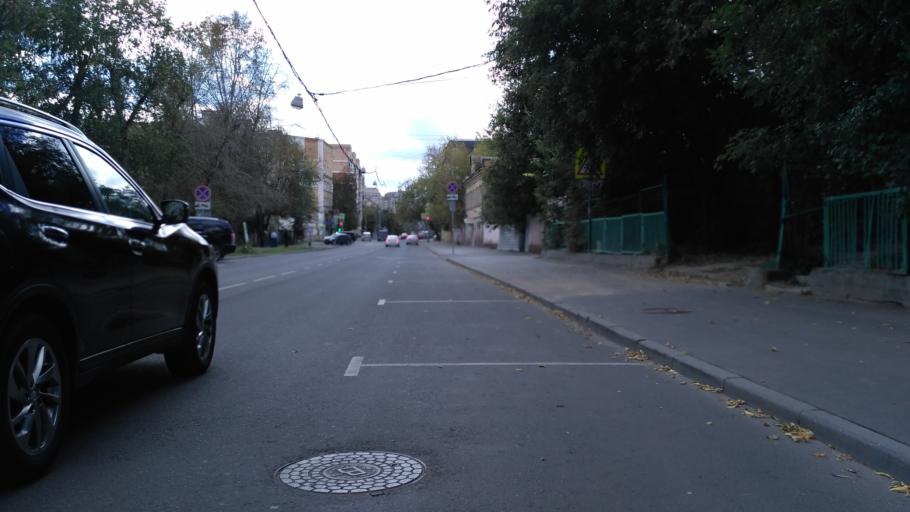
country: RU
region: Moscow
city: Lefortovo
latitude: 55.7776
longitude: 37.6954
